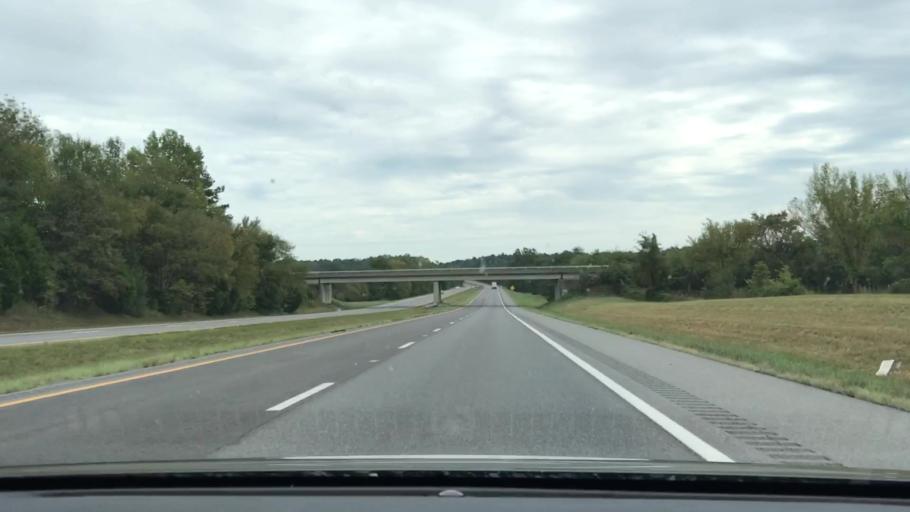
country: US
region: Kentucky
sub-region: Graves County
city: Mayfield
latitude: 36.7884
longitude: -88.5336
